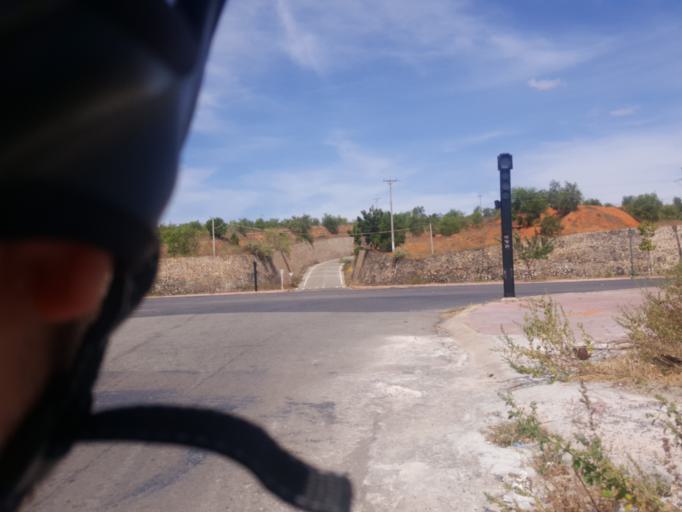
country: VN
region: Binh Thuan
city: Phan Thiet
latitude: 10.9571
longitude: 108.2148
